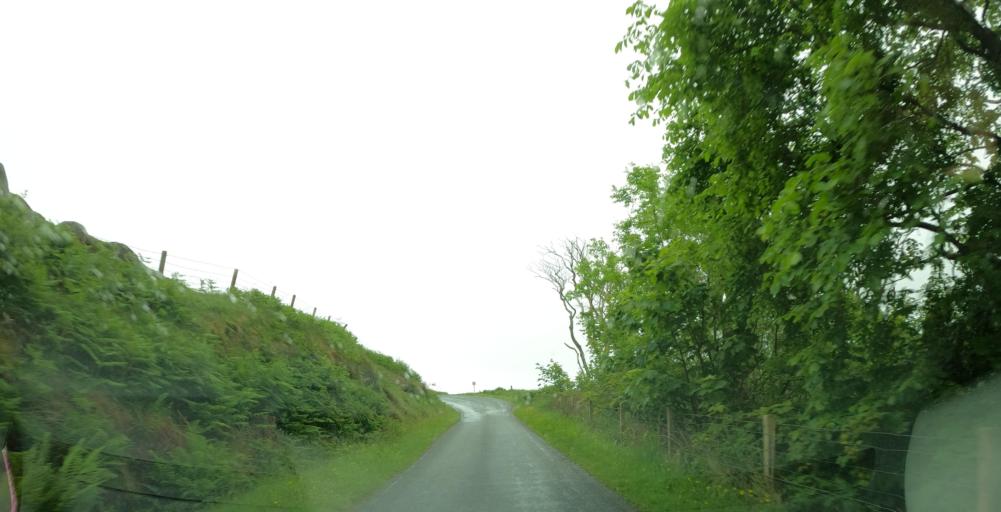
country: GB
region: Scotland
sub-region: Eilean Siar
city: Barra
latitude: 56.9616
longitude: -7.4507
